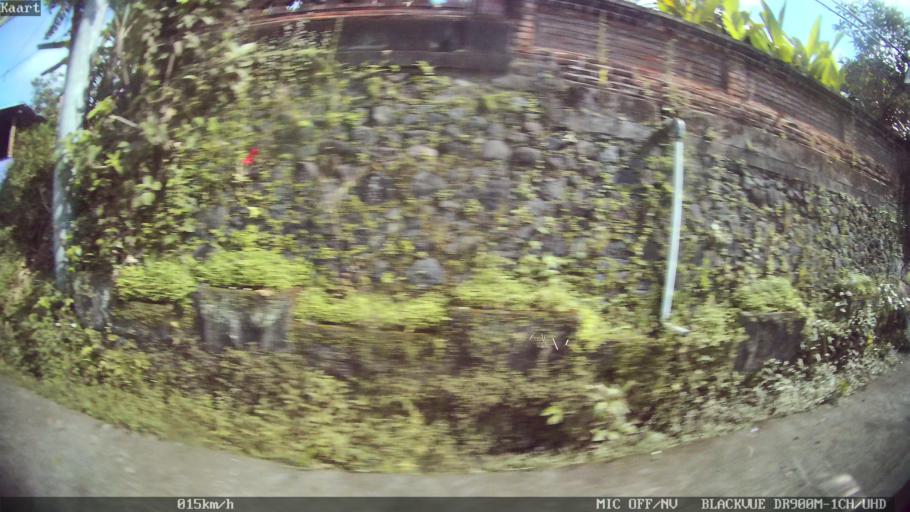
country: ID
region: Bali
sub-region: Kabupaten Gianyar
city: Ubud
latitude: -8.5113
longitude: 115.2869
